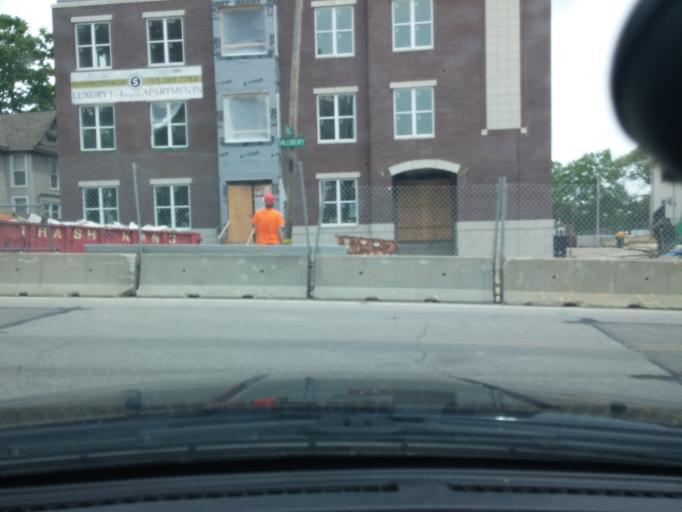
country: US
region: Indiana
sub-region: Tippecanoe County
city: West Lafayette
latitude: 40.4239
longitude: -86.9057
